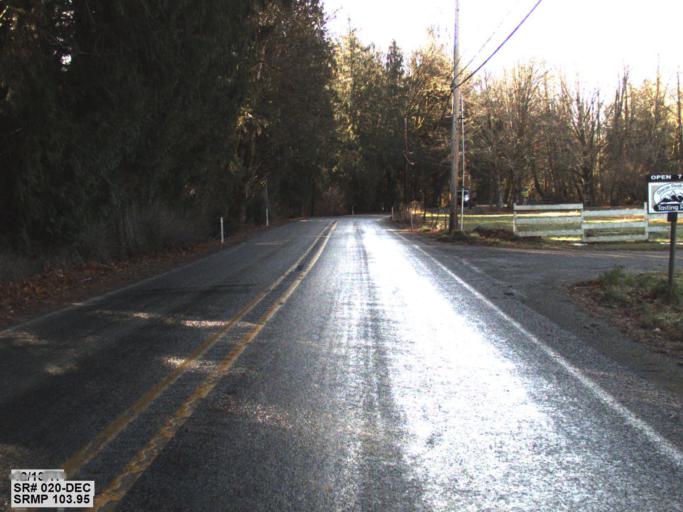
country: US
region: Washington
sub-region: Snohomish County
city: Darrington
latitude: 48.5140
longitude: -121.4670
